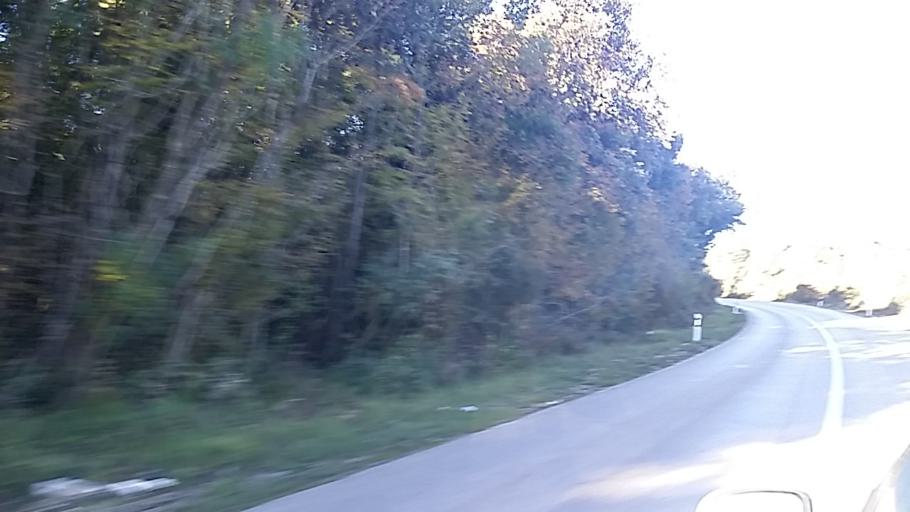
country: HR
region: Istarska
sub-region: Grad Rovinj
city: Rovinj
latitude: 45.1410
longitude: 13.7158
